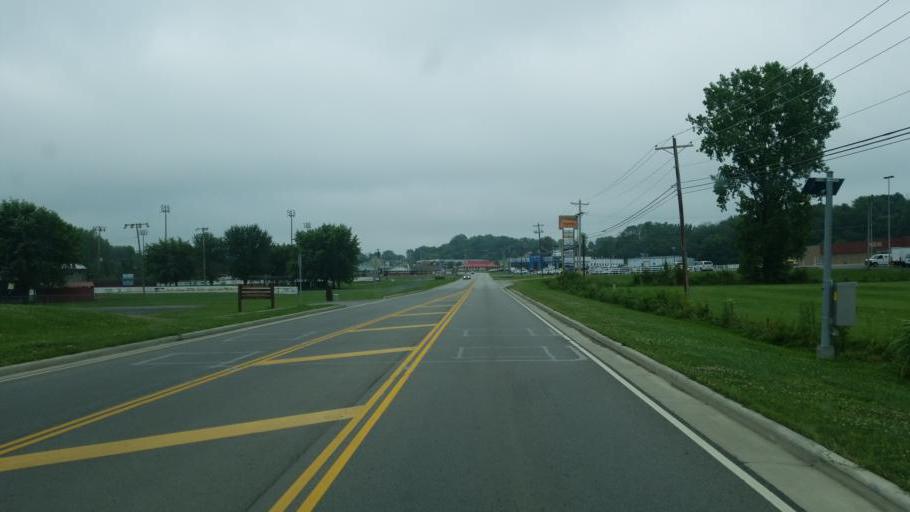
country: US
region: Ohio
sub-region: Highland County
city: Hillsboro
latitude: 39.2336
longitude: -83.6101
